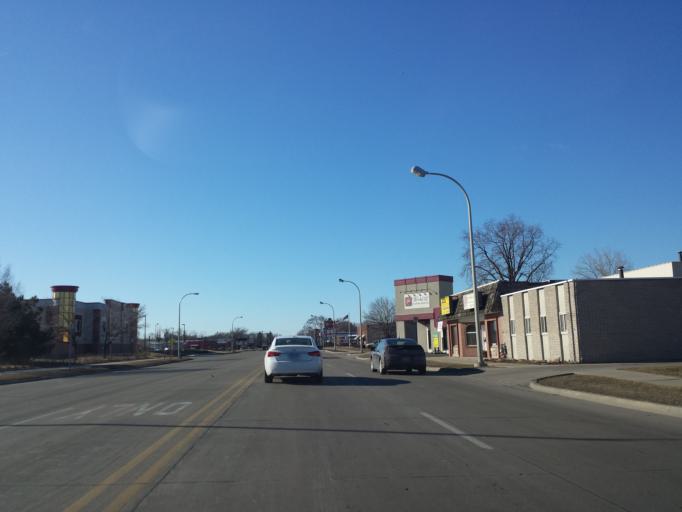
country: US
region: Michigan
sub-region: Oakland County
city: Clawson
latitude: 42.5479
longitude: -83.1470
